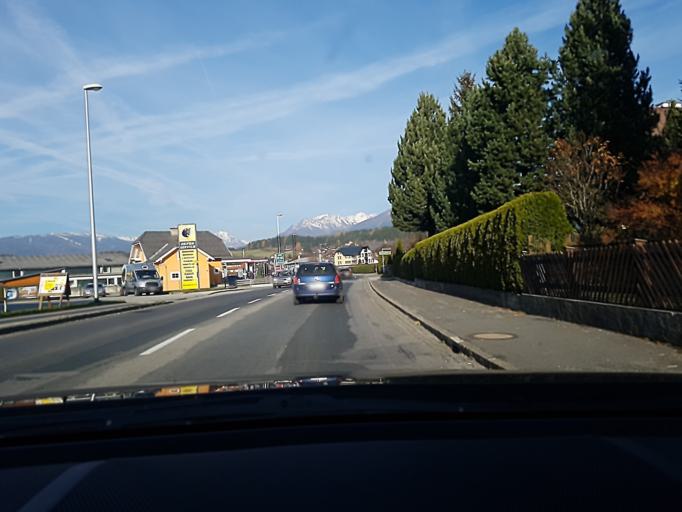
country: AT
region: Salzburg
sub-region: Politischer Bezirk Tamsweg
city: Tamsweg
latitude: 47.1321
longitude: 13.8062
